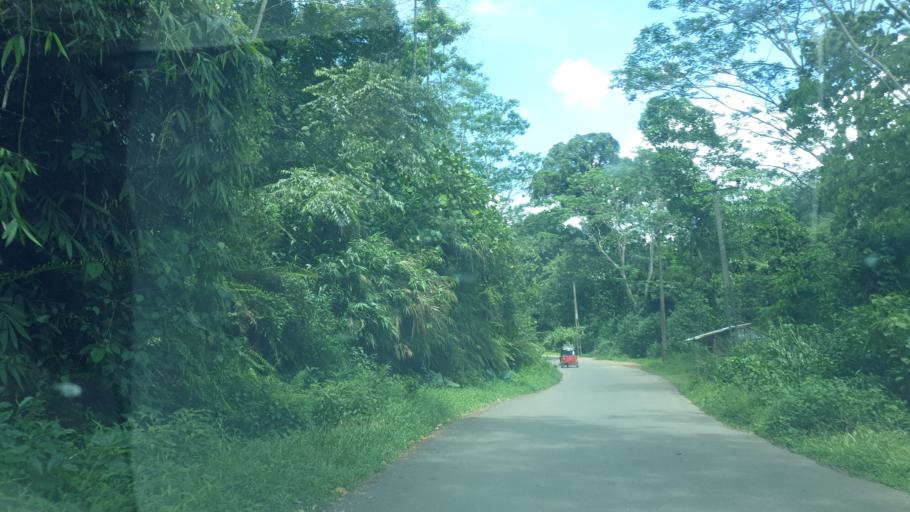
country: LK
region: Sabaragamuwa
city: Ratnapura
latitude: 6.4832
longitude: 80.4091
